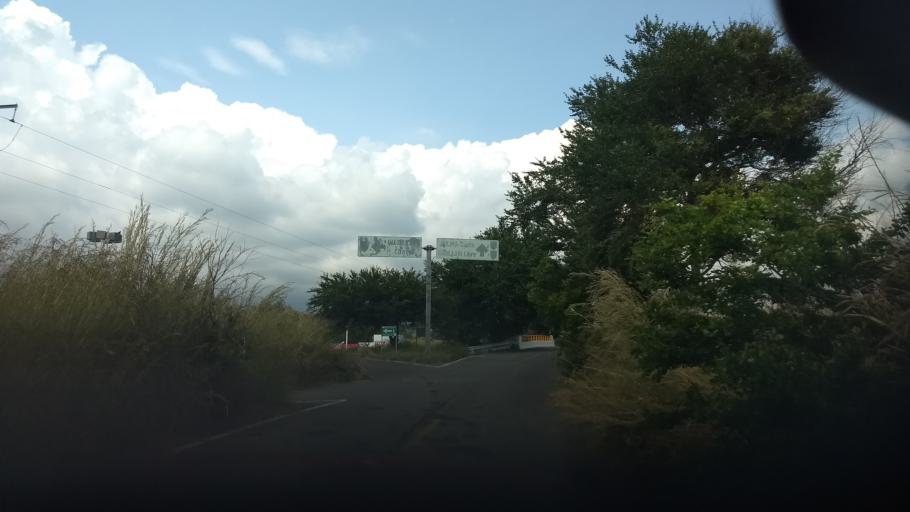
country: MX
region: Jalisco
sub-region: Tonila
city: San Marcos
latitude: 19.4331
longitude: -103.4934
